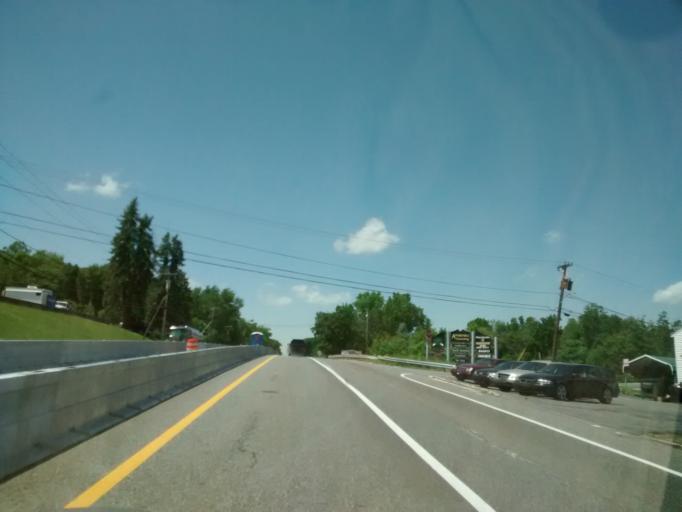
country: US
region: Massachusetts
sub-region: Worcester County
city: Sutton
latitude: 42.1662
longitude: -71.7455
